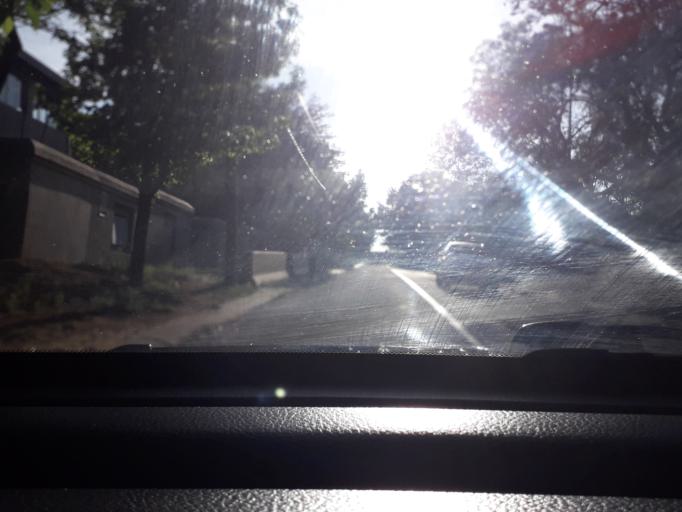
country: ZA
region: Gauteng
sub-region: City of Johannesburg Metropolitan Municipality
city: Modderfontein
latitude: -26.0837
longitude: 28.0839
